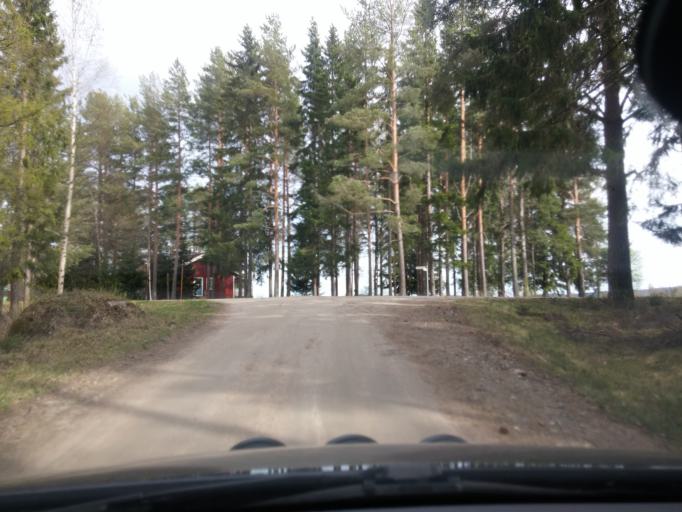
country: SE
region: Gaevleborg
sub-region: Ljusdals Kommun
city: Farila
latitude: 61.7902
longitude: 15.8947
